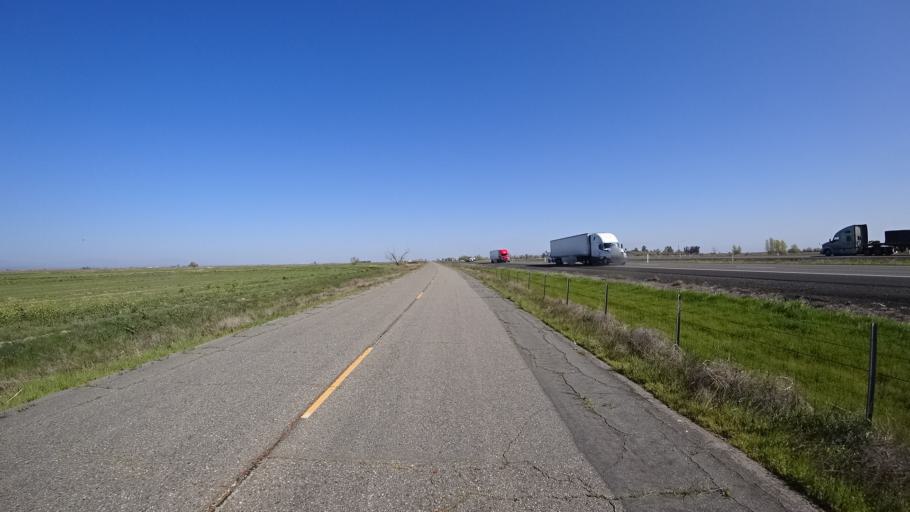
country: US
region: California
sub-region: Glenn County
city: Willows
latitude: 39.4199
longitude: -122.1938
